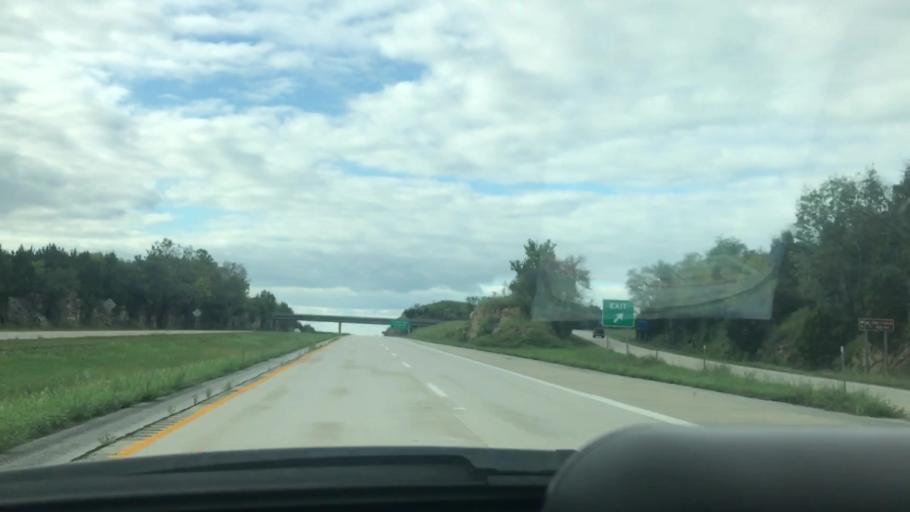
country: US
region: Missouri
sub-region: Benton County
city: Warsaw
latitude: 38.2507
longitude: -93.3626
